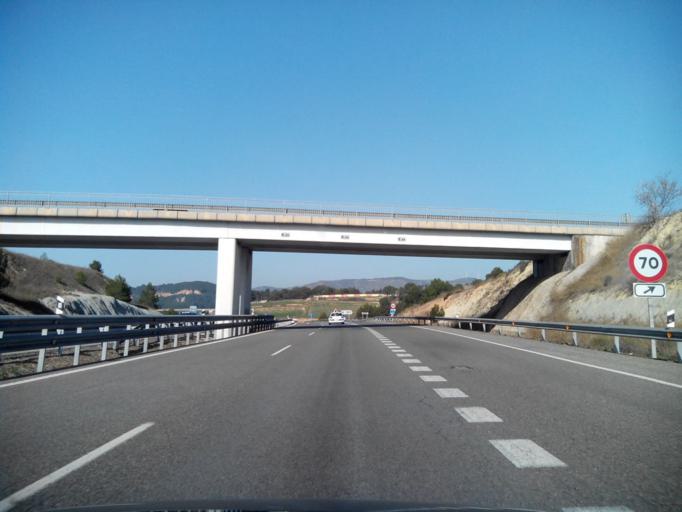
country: ES
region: Catalonia
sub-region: Provincia de Barcelona
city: Odena
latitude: 41.5928
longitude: 1.6504
